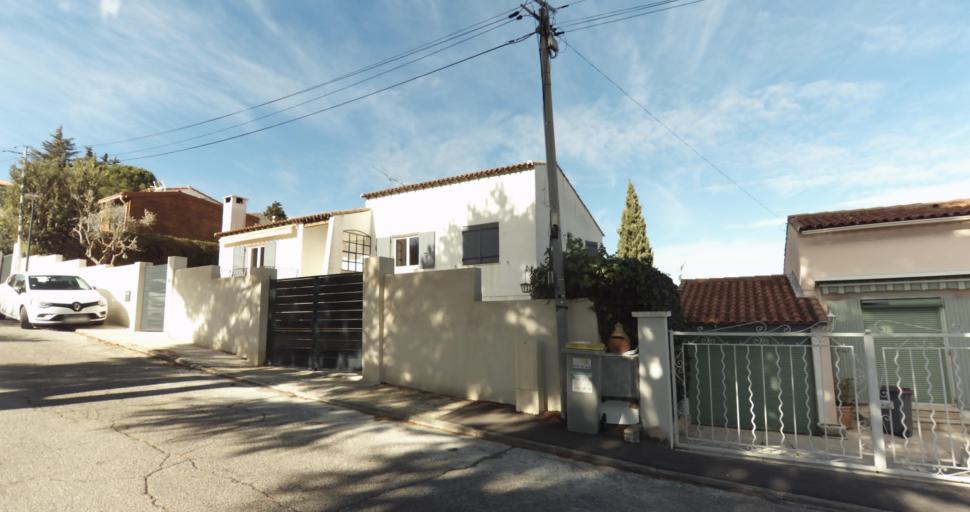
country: FR
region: Provence-Alpes-Cote d'Azur
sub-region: Departement des Bouches-du-Rhone
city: Venelles
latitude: 43.6003
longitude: 5.4843
